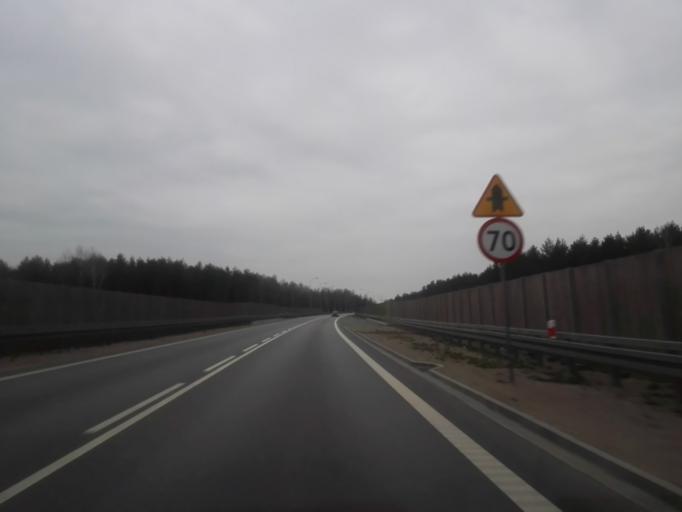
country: PL
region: Podlasie
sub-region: Powiat kolnenski
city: Stawiski
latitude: 53.3566
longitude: 22.1611
